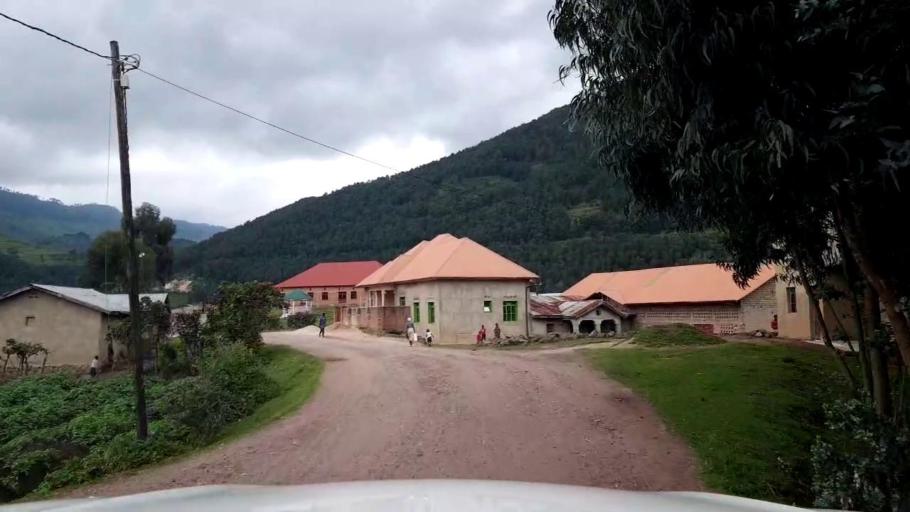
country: RW
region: Western Province
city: Gisenyi
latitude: -1.6426
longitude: 29.4090
